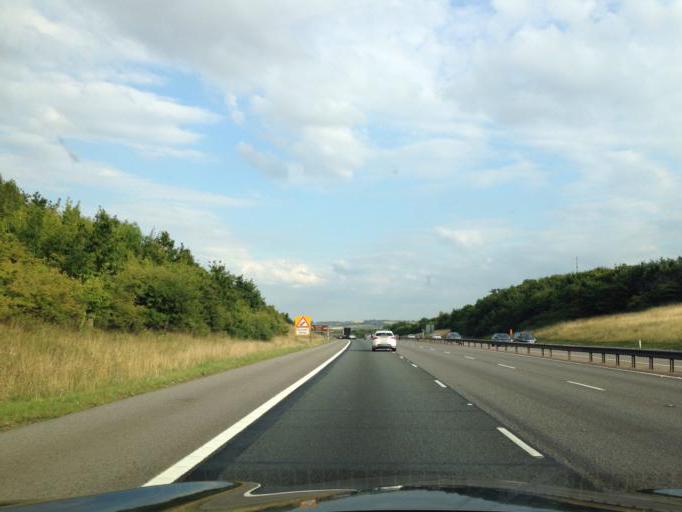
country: GB
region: England
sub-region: Warwickshire
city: Harbury
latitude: 52.1974
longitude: -1.4674
